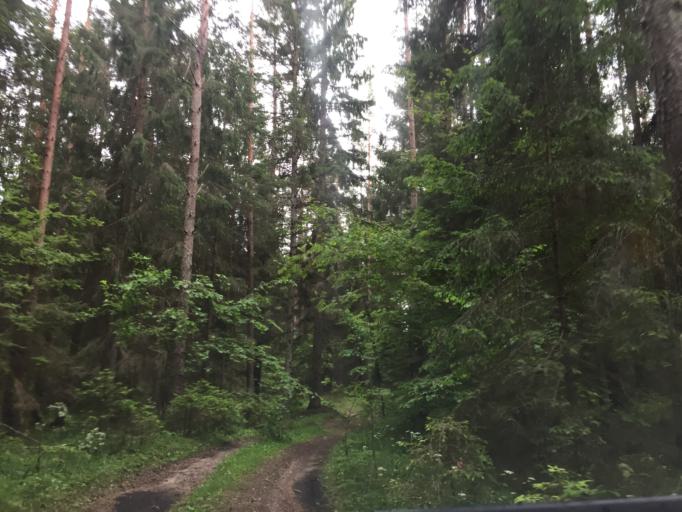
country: LV
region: Tukuma Rajons
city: Tukums
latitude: 57.0231
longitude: 23.0769
